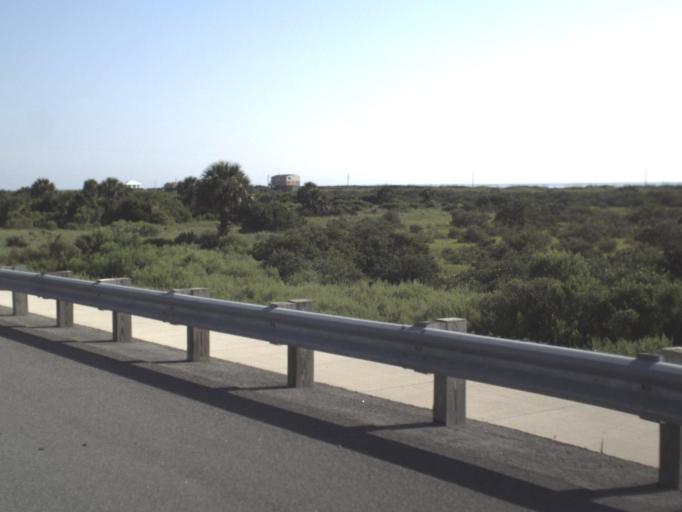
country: US
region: Florida
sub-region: Flagler County
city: Palm Coast
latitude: 29.6810
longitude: -81.2215
